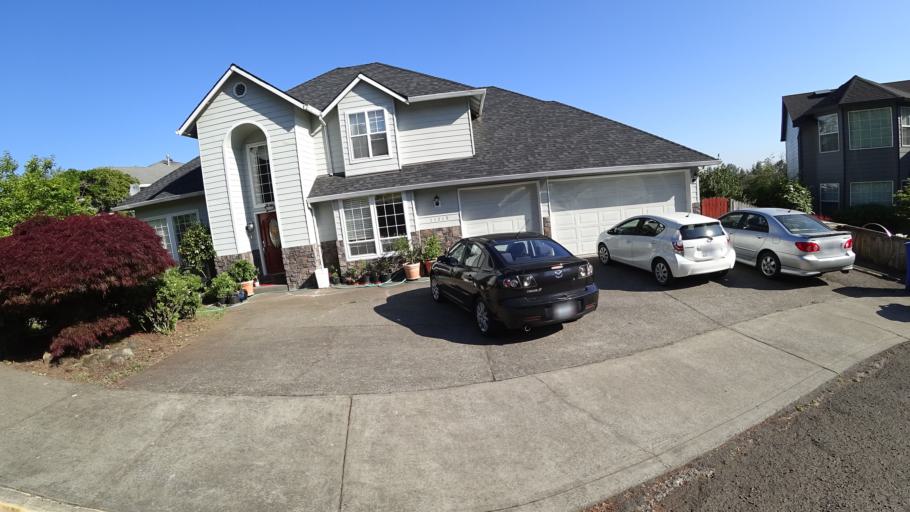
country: US
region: Oregon
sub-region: Multnomah County
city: Lents
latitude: 45.4716
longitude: -122.5462
